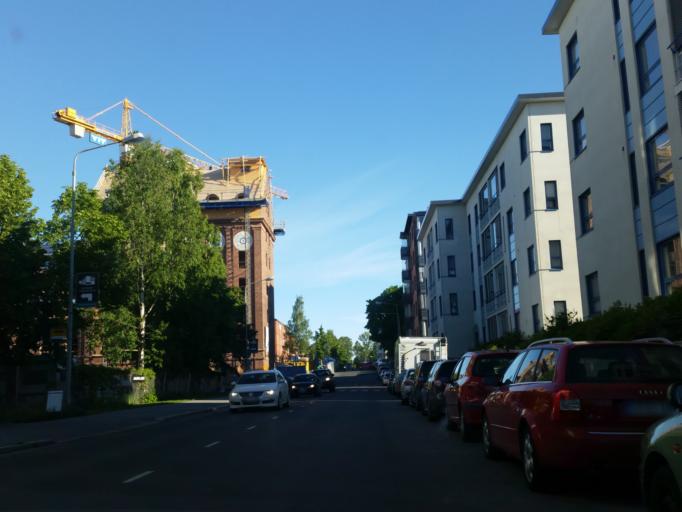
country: FI
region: Northern Savo
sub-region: Kuopio
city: Kuopio
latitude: 62.8911
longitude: 27.6932
